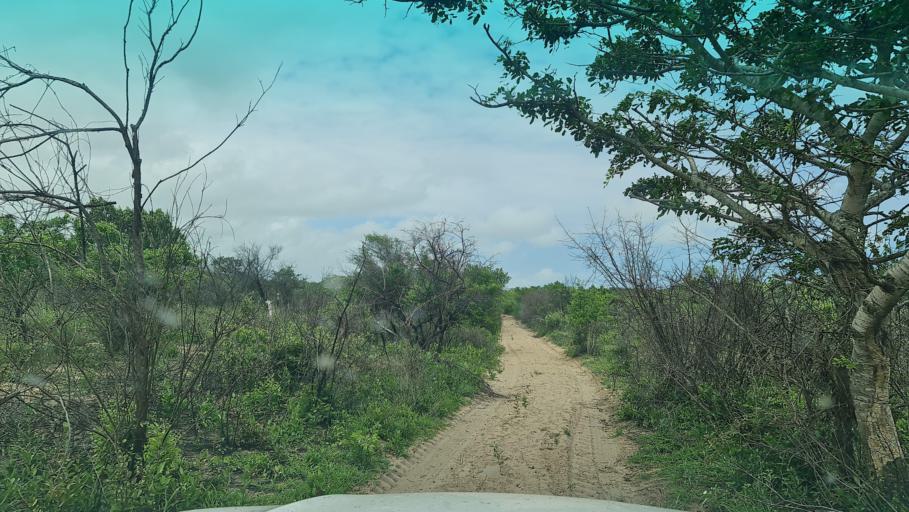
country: EG
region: Luxor
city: Luxor
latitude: 25.4961
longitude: 32.9028
